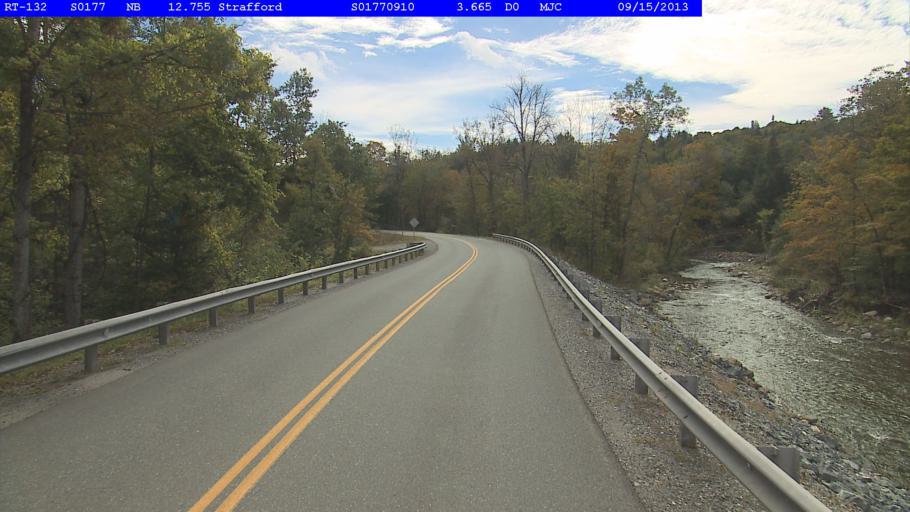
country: US
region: New Hampshire
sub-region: Grafton County
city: Hanover
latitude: 43.8379
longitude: -72.3386
